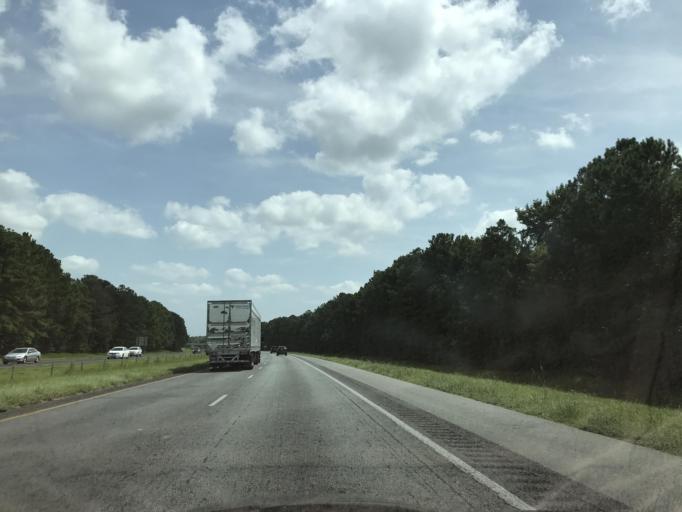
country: US
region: North Carolina
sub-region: Duplin County
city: Warsaw
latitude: 34.9750
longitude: -78.1249
